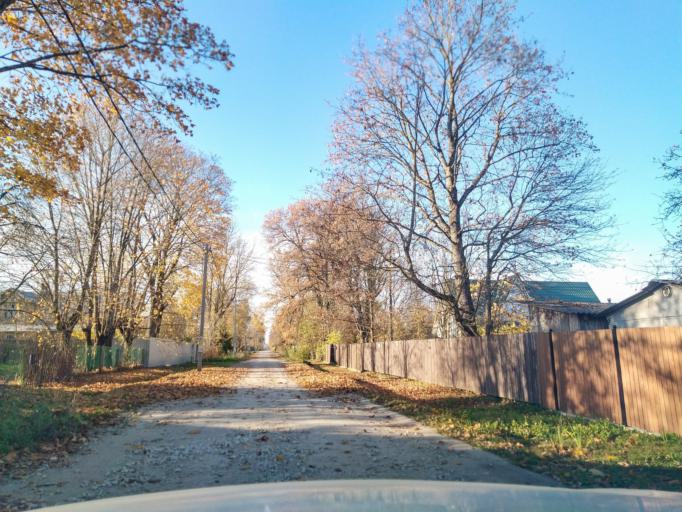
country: RU
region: Leningrad
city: Siverskiy
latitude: 59.3241
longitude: 30.0441
